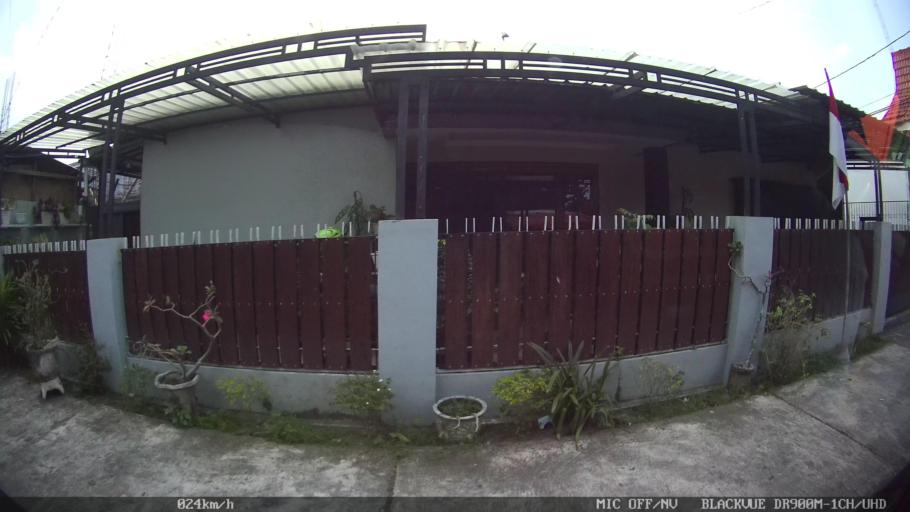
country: ID
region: Daerah Istimewa Yogyakarta
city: Yogyakarta
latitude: -7.8138
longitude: 110.4002
